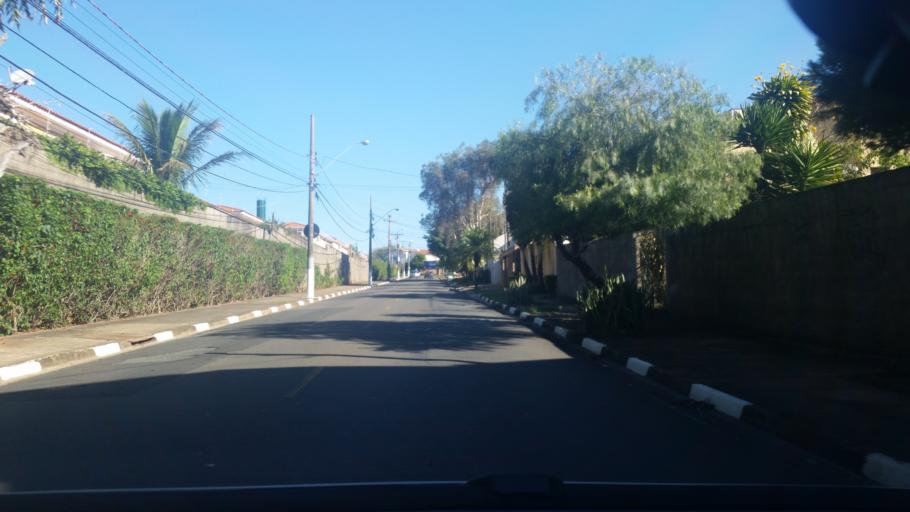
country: BR
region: Sao Paulo
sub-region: Campinas
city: Campinas
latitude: -22.8622
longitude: -47.0538
